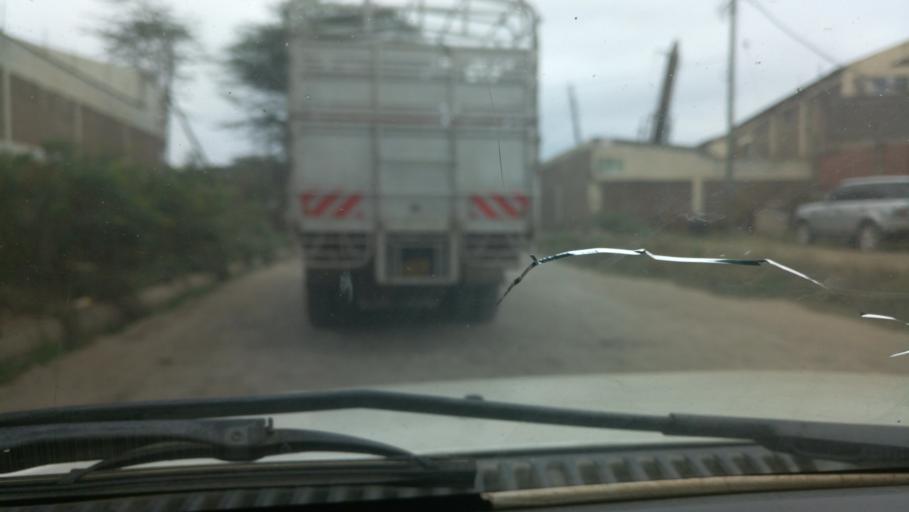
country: KE
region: Nairobi Area
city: Pumwani
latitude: -1.3322
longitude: 36.8675
